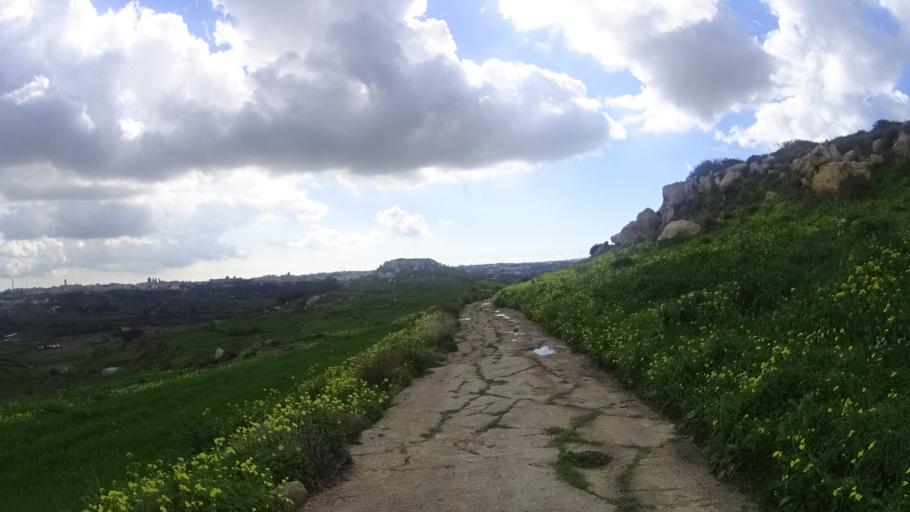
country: MT
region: L-Imtarfa
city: Imtarfa
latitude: 35.9020
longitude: 14.3841
